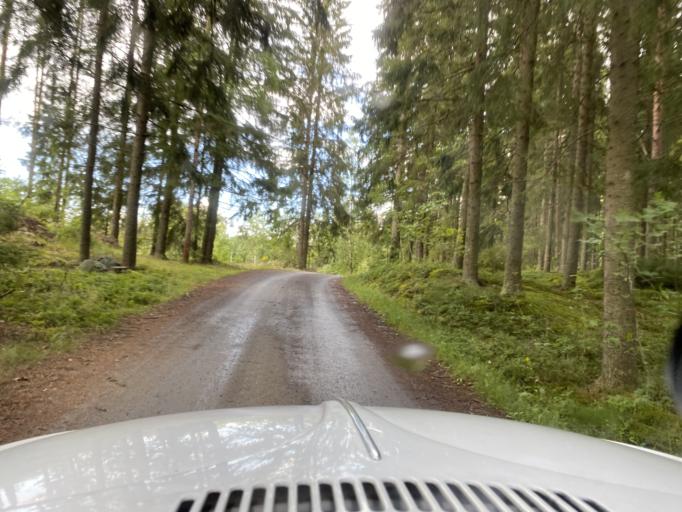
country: FI
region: Pirkanmaa
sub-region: Lounais-Pirkanmaa
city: Punkalaidun
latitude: 61.1301
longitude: 23.0660
